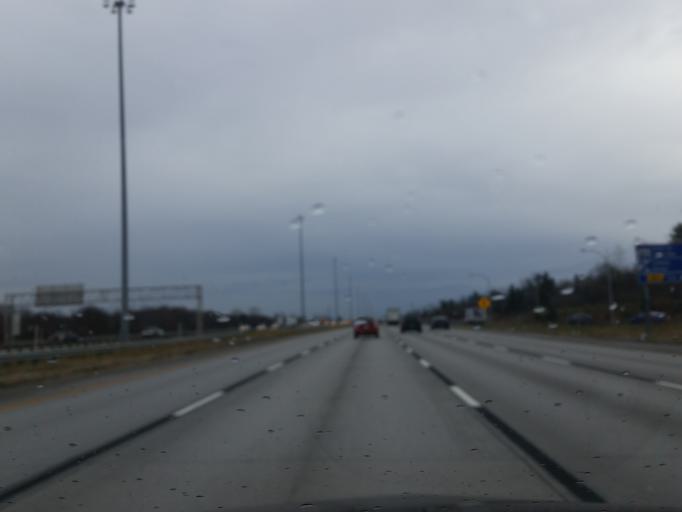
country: CA
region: Quebec
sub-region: Laurentides
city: Blainville
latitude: 45.6546
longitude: -73.8805
